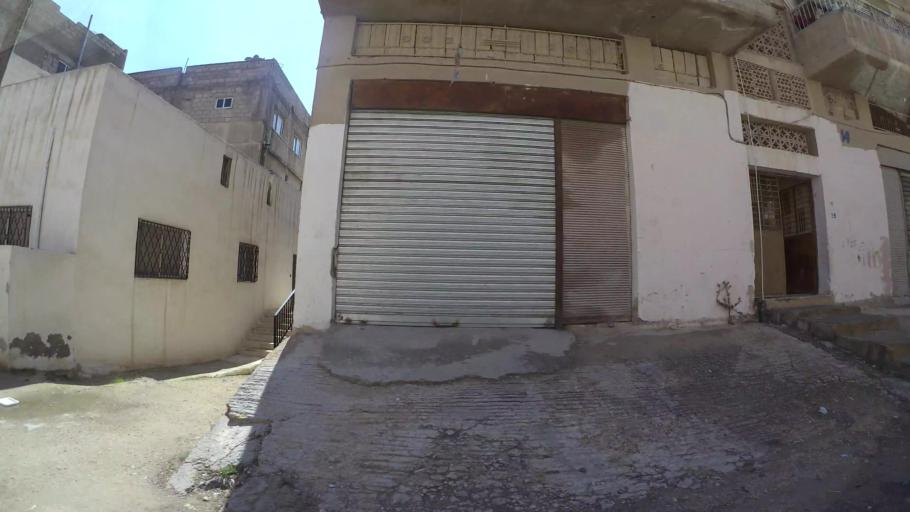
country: JO
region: Zarqa
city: Russeifa
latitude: 31.9813
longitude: 36.0016
